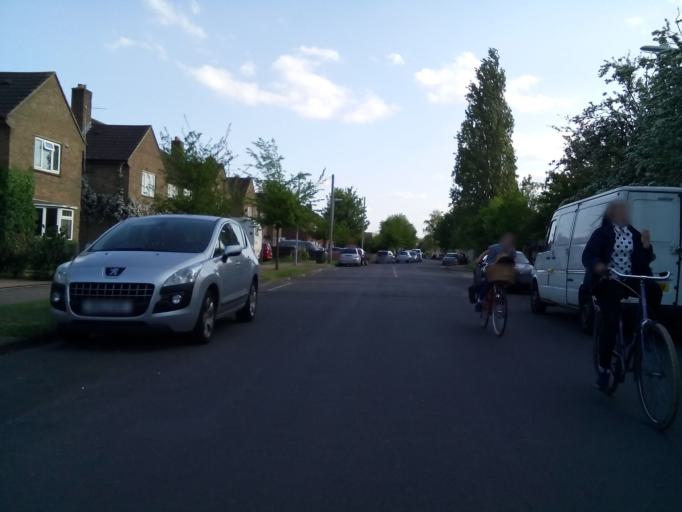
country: GB
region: England
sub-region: Cambridgeshire
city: Cambridge
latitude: 52.1930
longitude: 0.1412
